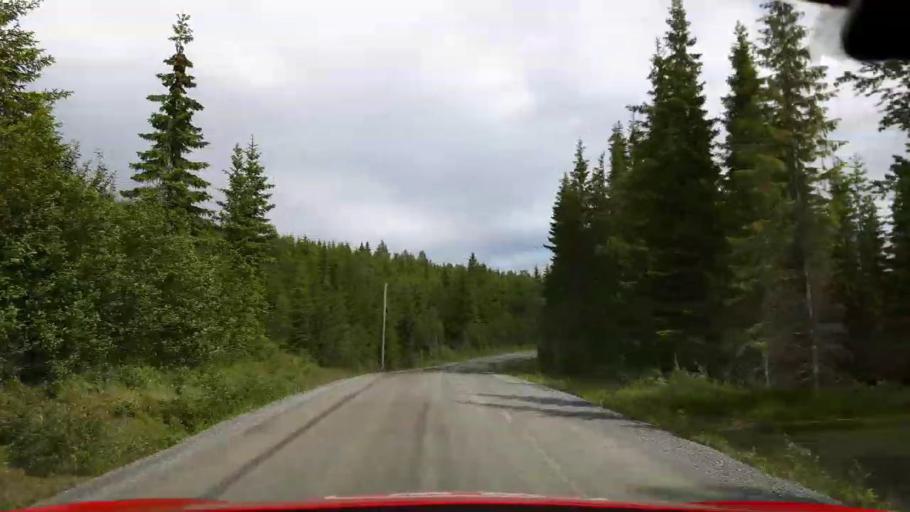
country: NO
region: Nord-Trondelag
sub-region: Lierne
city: Sandvika
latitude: 64.1447
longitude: 13.9068
